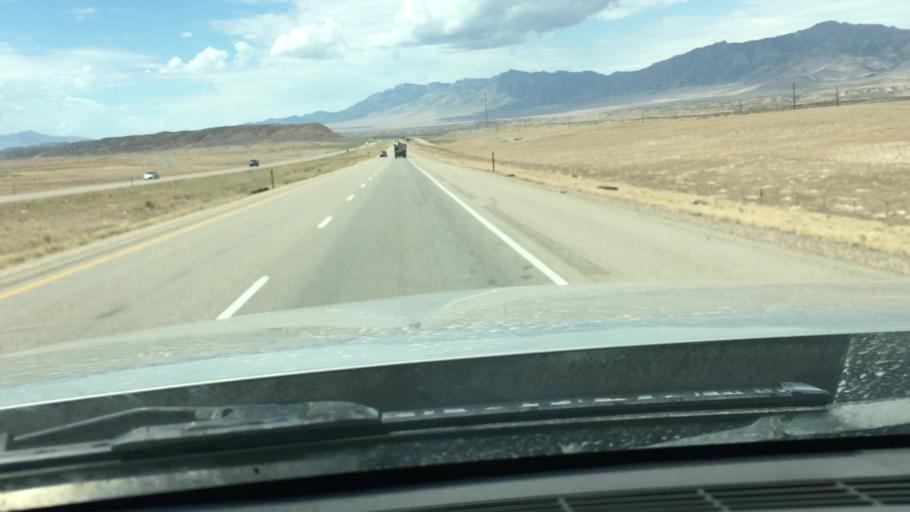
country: US
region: Utah
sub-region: Juab County
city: Nephi
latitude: 39.4596
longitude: -112.0063
